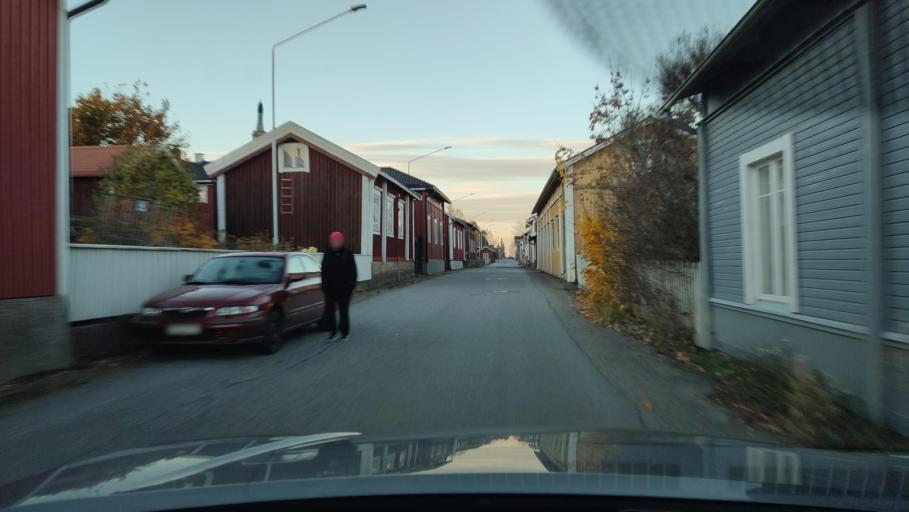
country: FI
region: Ostrobothnia
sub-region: Sydosterbotten
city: Kristinestad
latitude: 62.2698
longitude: 21.3732
